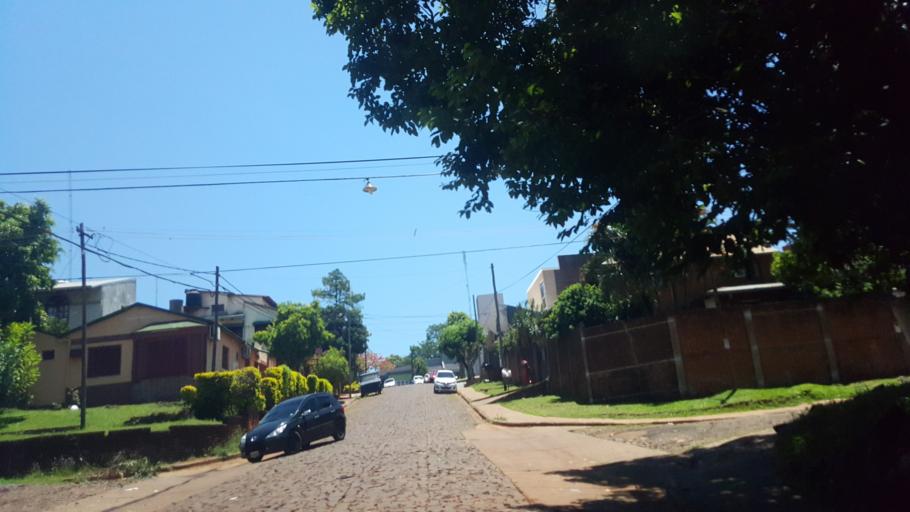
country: AR
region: Misiones
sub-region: Departamento de Capital
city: Posadas
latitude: -27.3923
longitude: -55.9112
